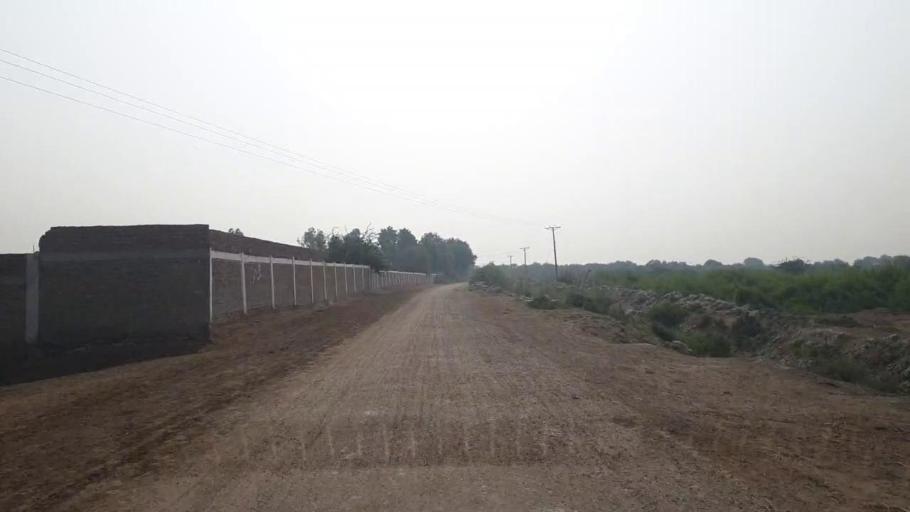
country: PK
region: Sindh
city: Tando Muhammad Khan
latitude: 25.2688
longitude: 68.5090
